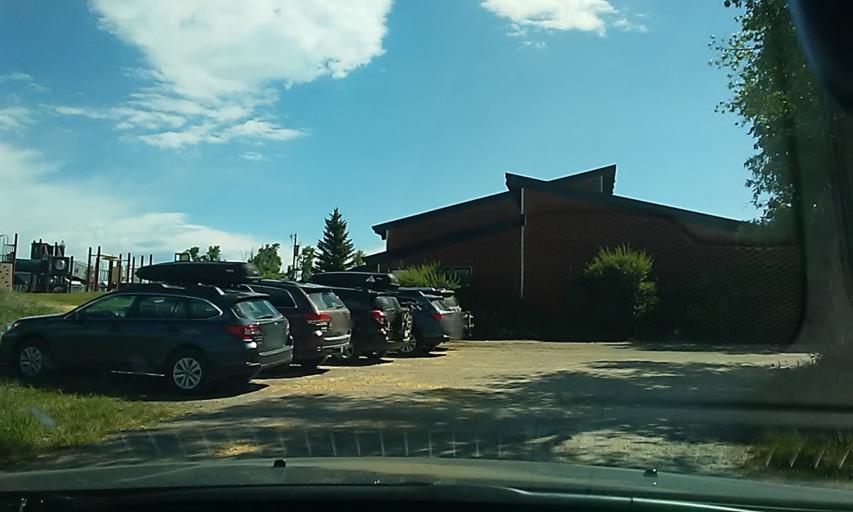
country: US
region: Wyoming
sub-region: Teton County
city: Jackson
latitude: 43.6223
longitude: -110.6289
